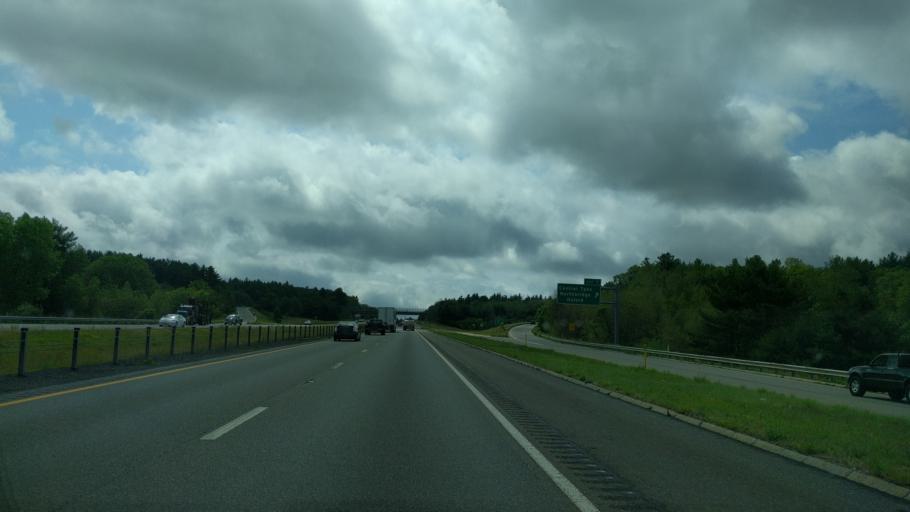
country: US
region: Massachusetts
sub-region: Worcester County
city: Sutton
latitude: 42.1531
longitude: -71.7264
